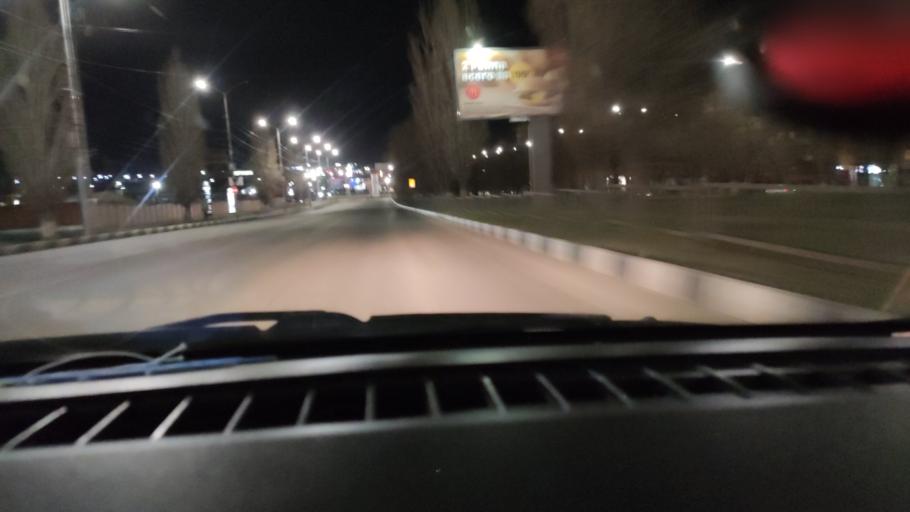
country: RU
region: Saratov
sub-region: Saratovskiy Rayon
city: Saratov
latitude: 51.6126
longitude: 45.9705
